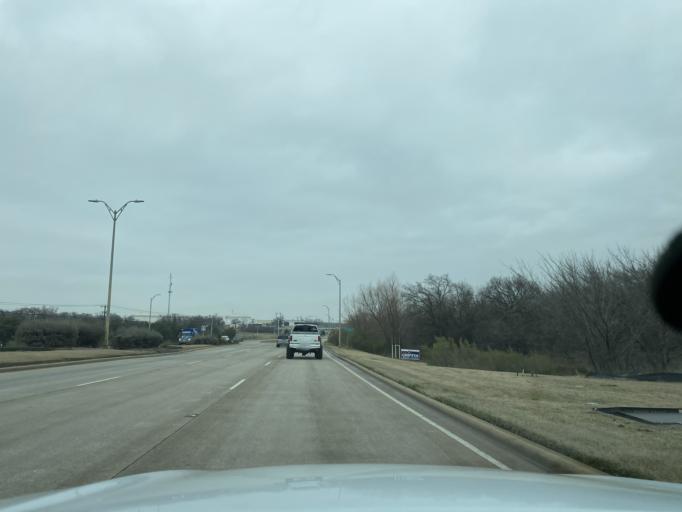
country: US
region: Texas
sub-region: Tarrant County
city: Euless
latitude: 32.8049
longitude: -97.0992
